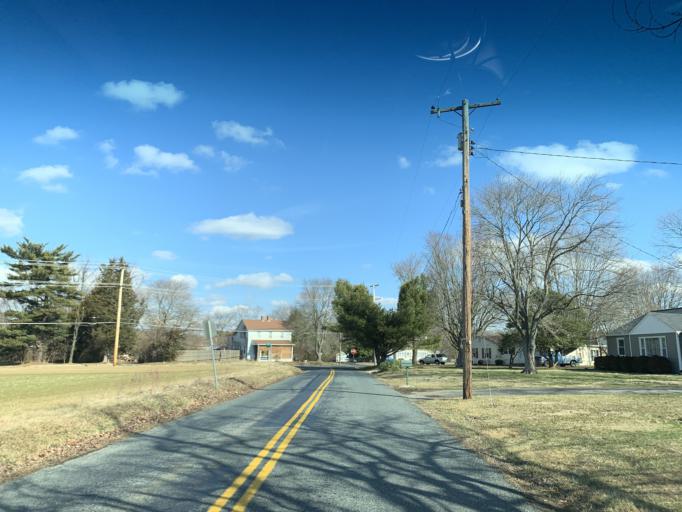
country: US
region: Maryland
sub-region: Harford County
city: Aberdeen
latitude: 39.5631
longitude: -76.1978
